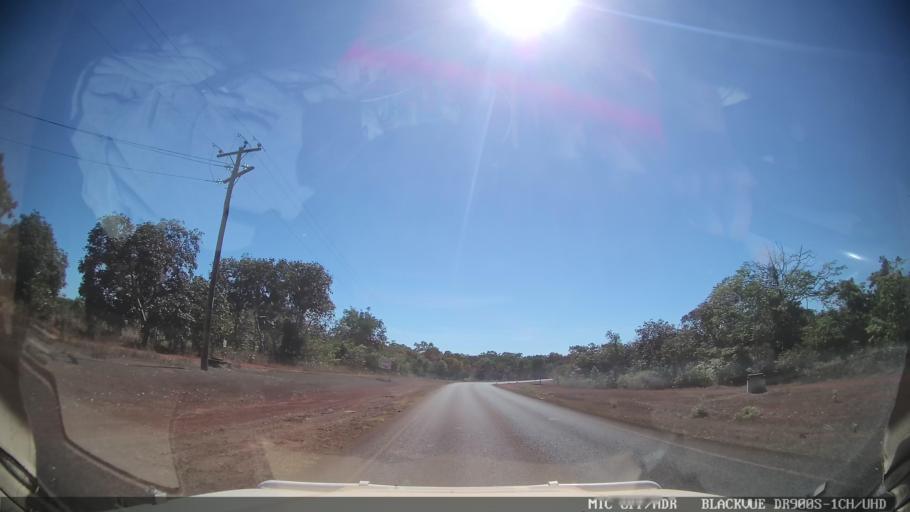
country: AU
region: Queensland
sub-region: Torres
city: Thursday Island
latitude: -10.8978
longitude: 142.3379
